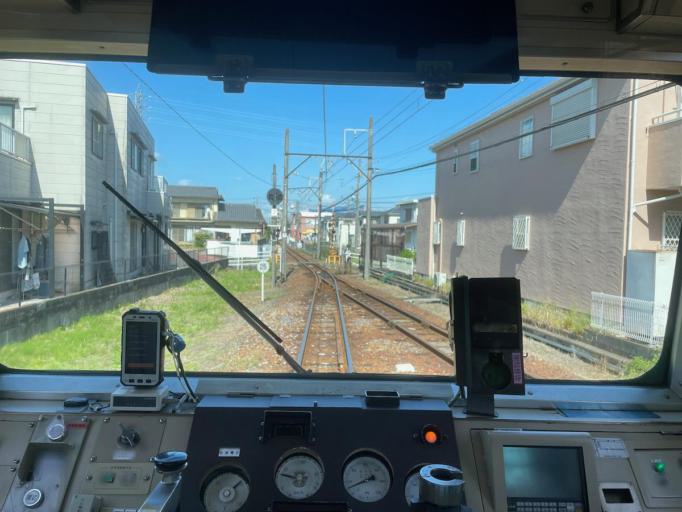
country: JP
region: Mie
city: Yokkaichi
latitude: 34.9408
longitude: 136.5986
